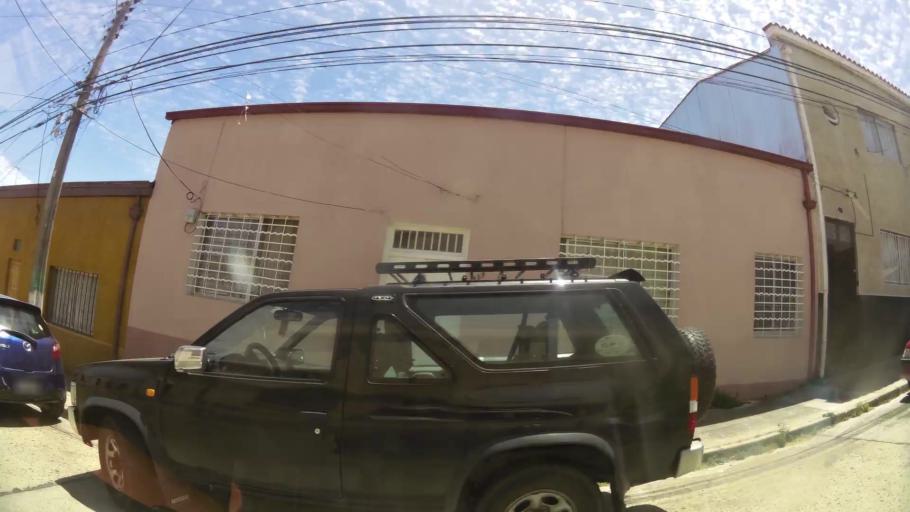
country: CL
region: Valparaiso
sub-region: Provincia de Valparaiso
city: Valparaiso
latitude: -33.0387
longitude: -71.5950
